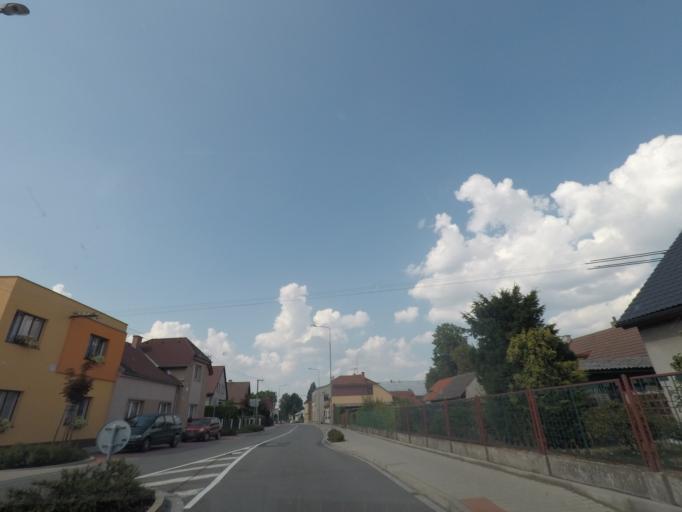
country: CZ
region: Pardubicky
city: Horni Jeleni
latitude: 50.0498
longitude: 16.0841
